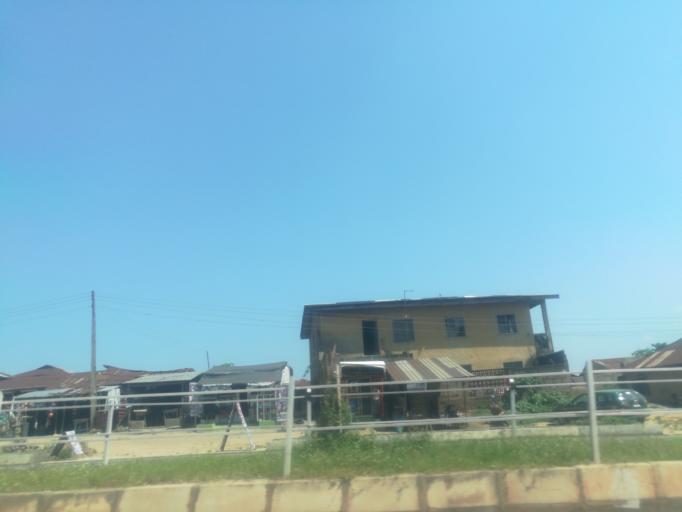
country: NG
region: Ogun
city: Abeokuta
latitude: 7.1675
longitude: 3.3515
